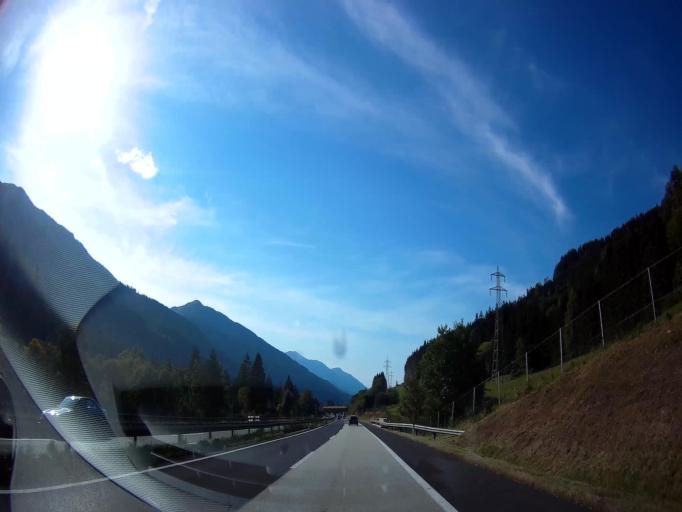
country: AT
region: Styria
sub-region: Politischer Bezirk Leoben
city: Wald am Schoberpass
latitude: 47.4687
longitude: 14.6380
